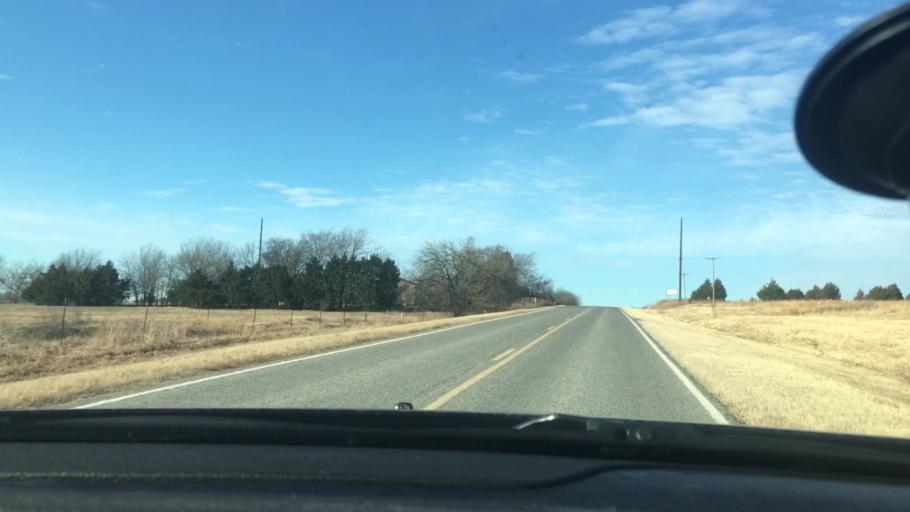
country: US
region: Oklahoma
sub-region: Seminole County
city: Konawa
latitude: 34.9856
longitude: -96.8070
